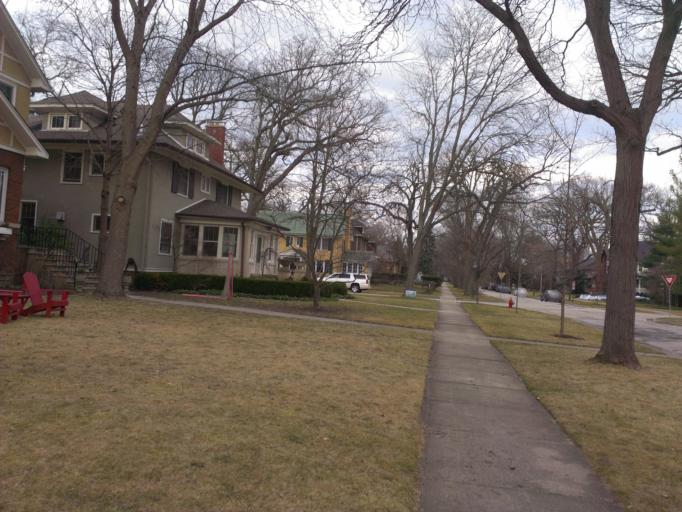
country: US
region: Illinois
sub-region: Cook County
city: Kenilworth
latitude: 42.0777
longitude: -87.6944
